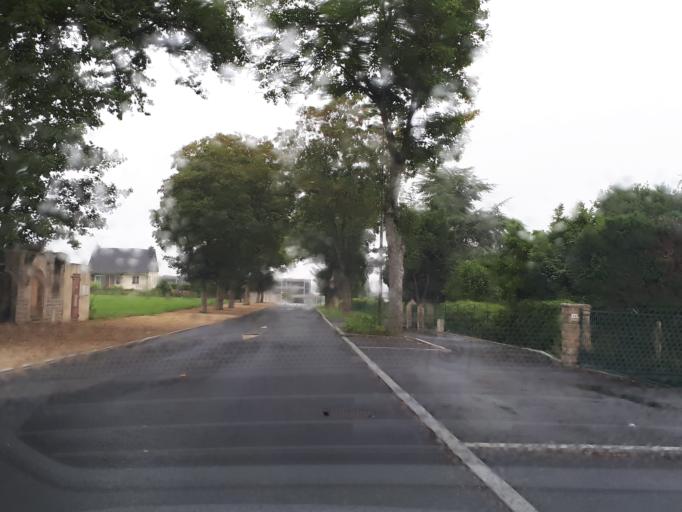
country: FR
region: Brittany
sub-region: Departement des Cotes-d'Armor
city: Broons
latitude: 48.3216
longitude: -2.2640
